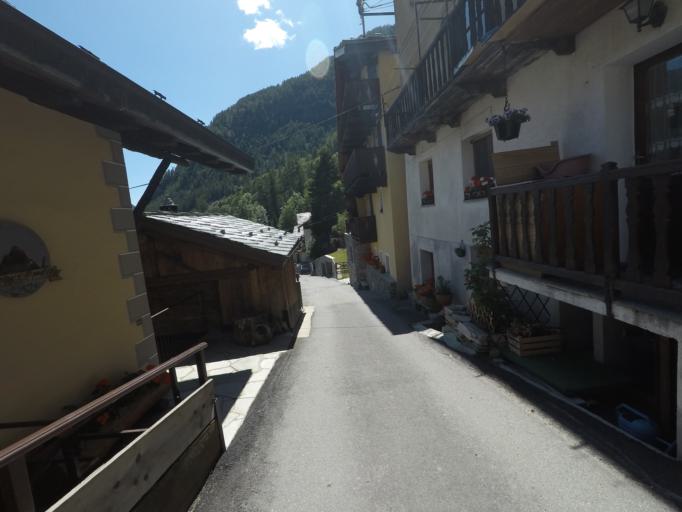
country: IT
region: Aosta Valley
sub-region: Valle d'Aosta
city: Paquier
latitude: 45.8863
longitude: 7.6222
